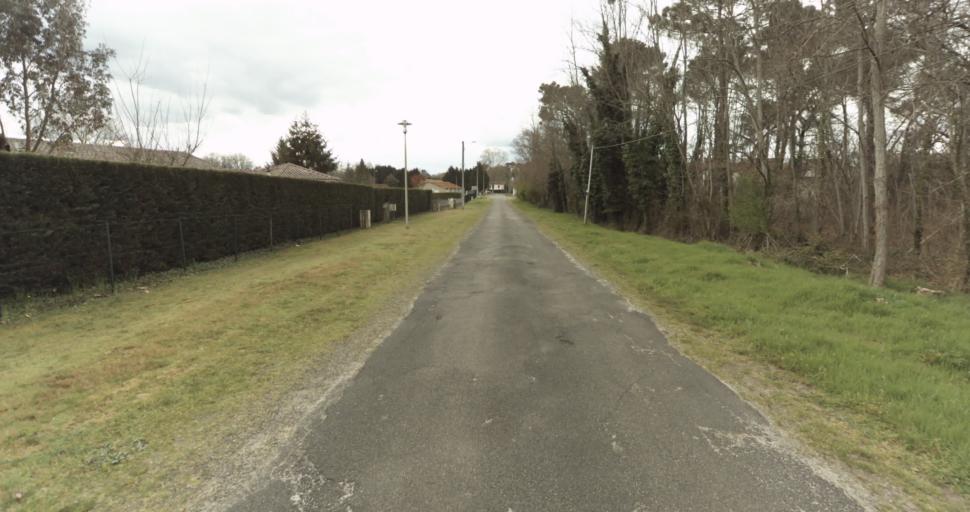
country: FR
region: Aquitaine
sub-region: Departement des Landes
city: Roquefort
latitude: 44.0418
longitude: -0.3187
